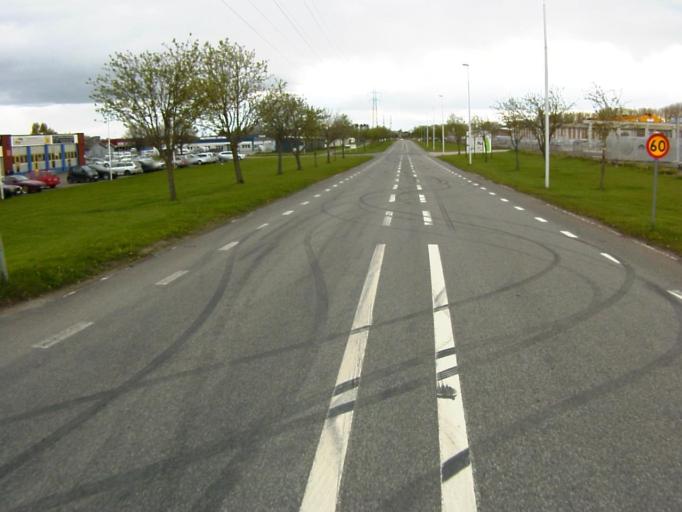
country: SE
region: Skane
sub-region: Kristianstads Kommun
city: Kristianstad
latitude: 56.0600
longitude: 14.1734
